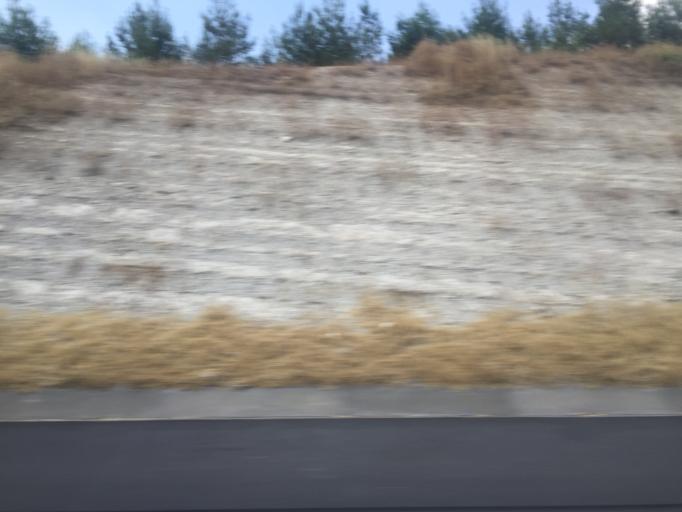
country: TR
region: Sanliurfa
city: Akziyaret
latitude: 37.2683
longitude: 38.7868
